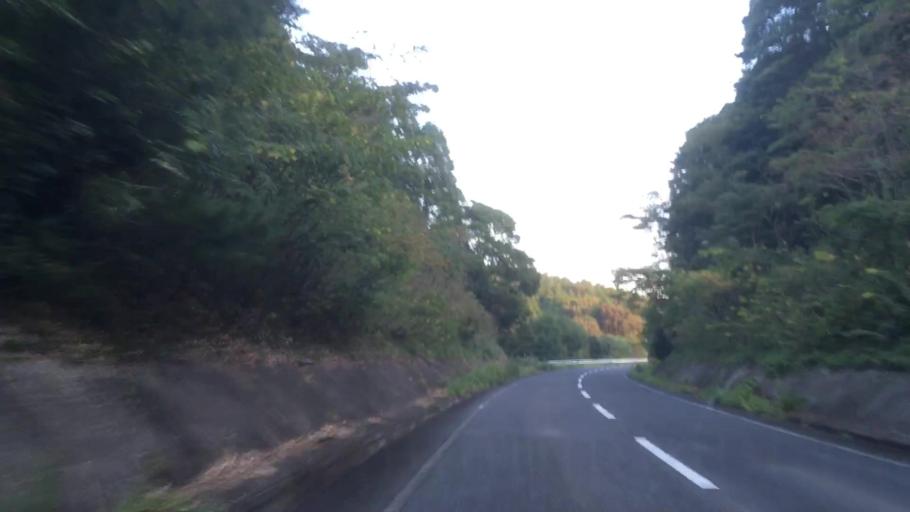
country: JP
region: Nagasaki
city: Sasebo
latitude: 33.0254
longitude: 129.6968
